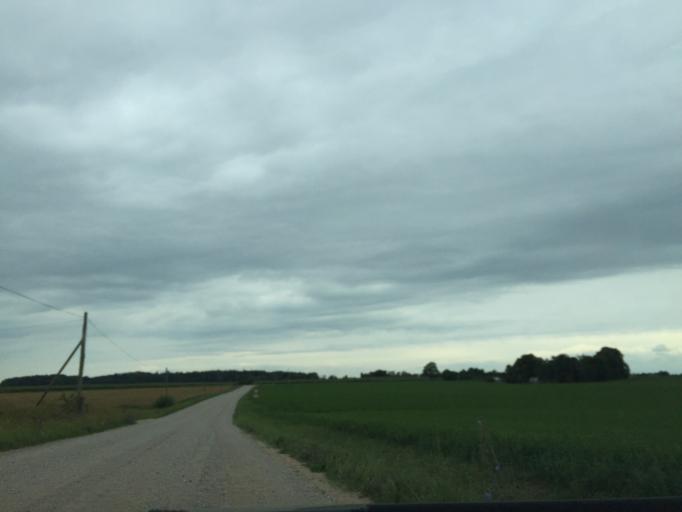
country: LV
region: Jaunpils
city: Jaunpils
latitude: 56.7237
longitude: 23.0466
